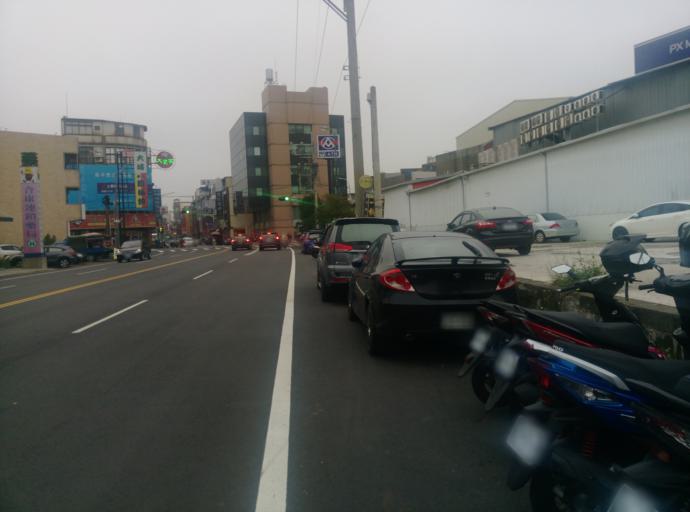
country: TW
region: Taiwan
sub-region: Miaoli
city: Miaoli
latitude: 24.6871
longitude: 120.8722
